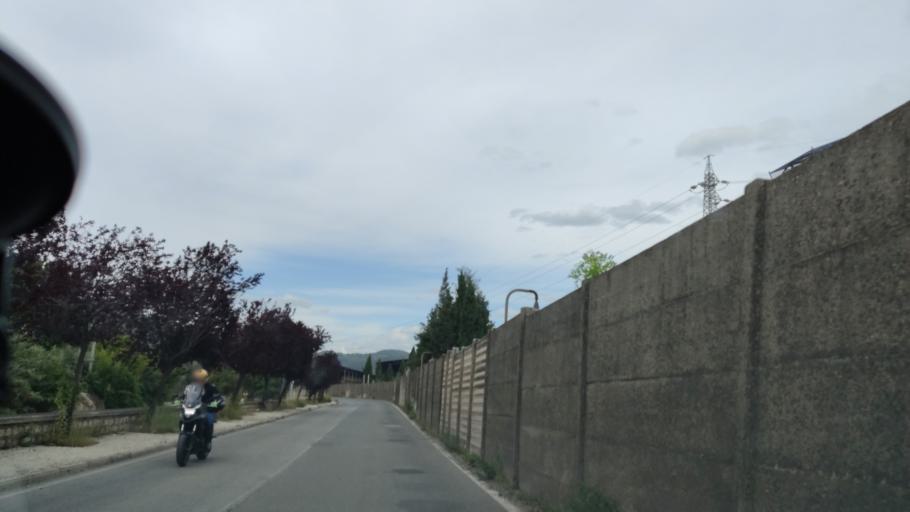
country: IT
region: Umbria
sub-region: Provincia di Terni
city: Terni
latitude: 42.5695
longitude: 12.6686
